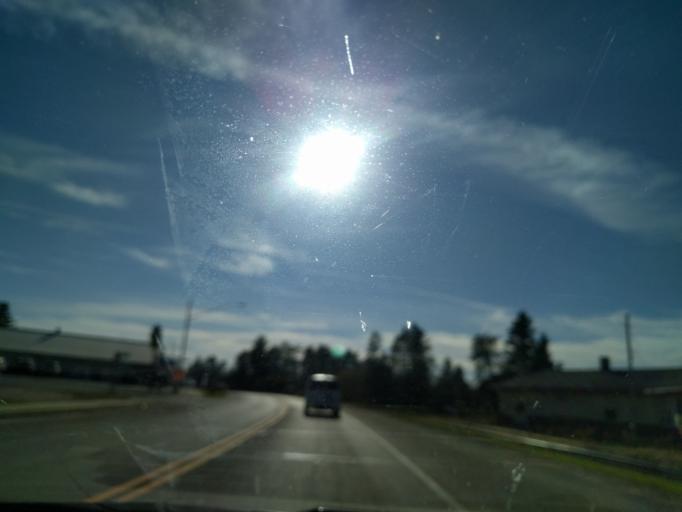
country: US
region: Wisconsin
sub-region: Marinette County
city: Niagara
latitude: 45.6353
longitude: -87.9902
